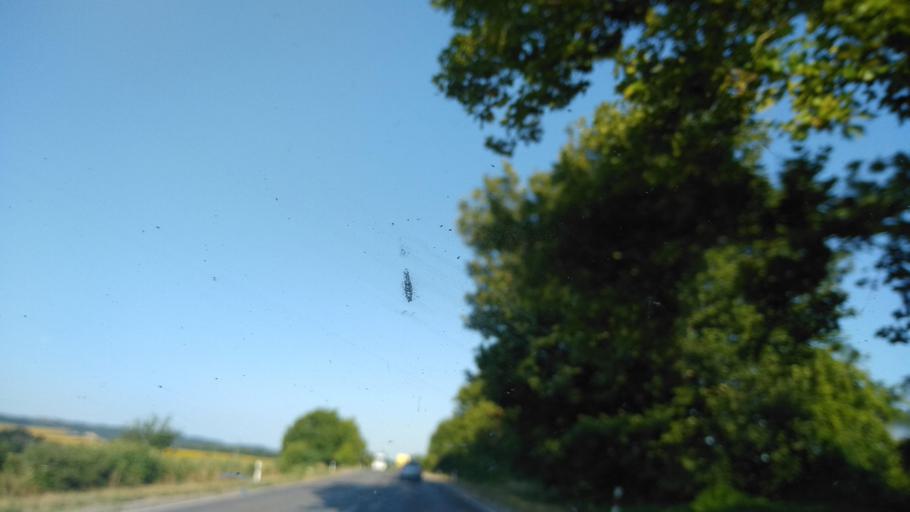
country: BG
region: Gabrovo
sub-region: Obshtina Dryanovo
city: Dryanovo
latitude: 43.0869
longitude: 25.4396
